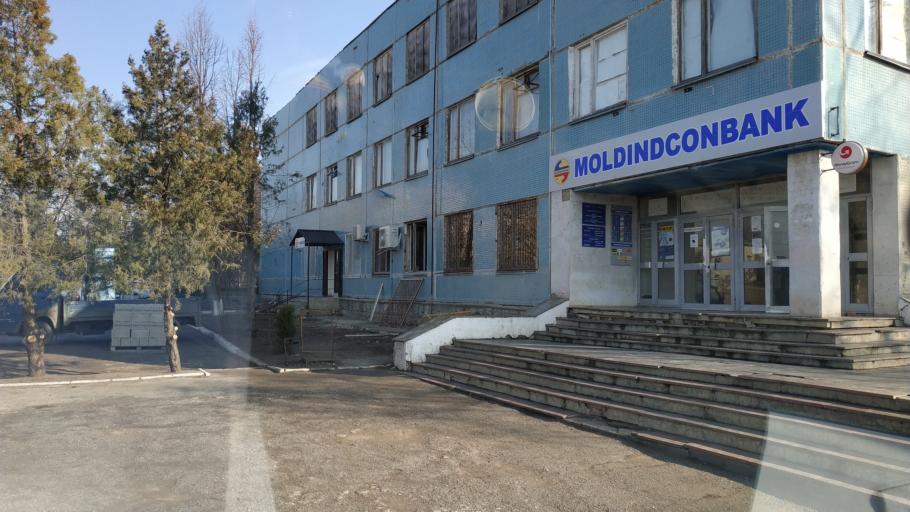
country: MD
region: Chisinau
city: Singera
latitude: 46.6844
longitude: 29.0576
